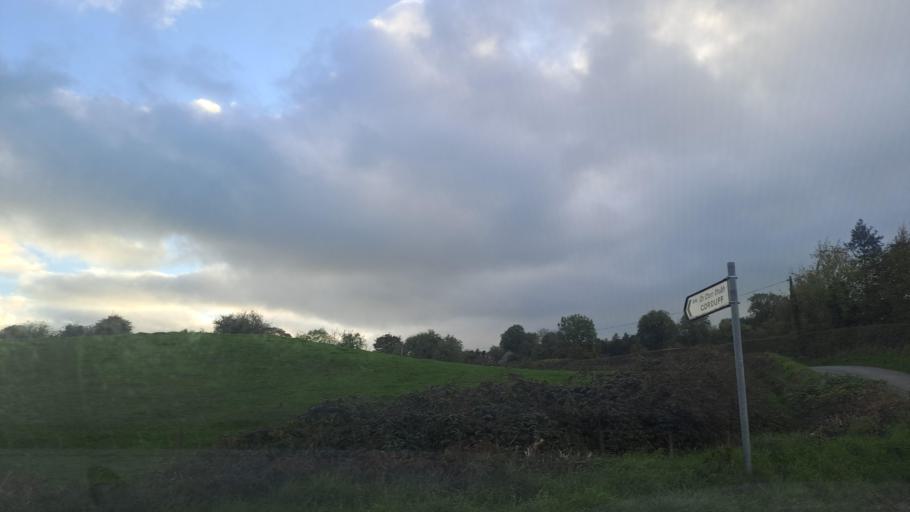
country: IE
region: Ulster
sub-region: County Monaghan
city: Carrickmacross
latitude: 54.0339
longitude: -6.8128
